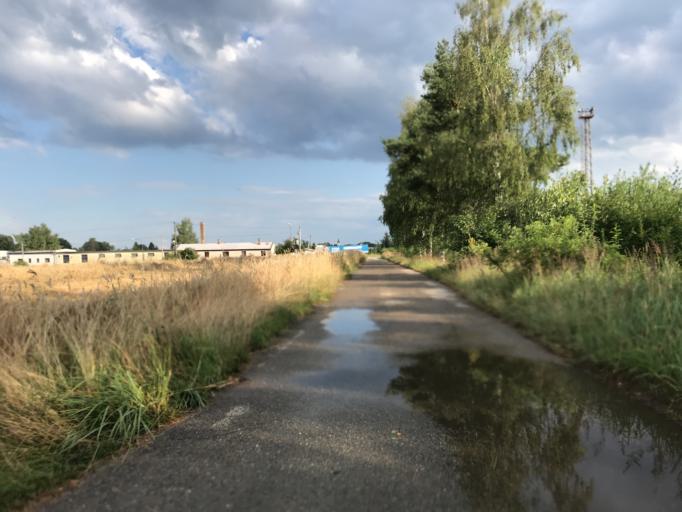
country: CZ
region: Jihocesky
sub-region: Okres Jindrichuv Hradec
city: Trebon
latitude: 49.0206
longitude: 14.7593
